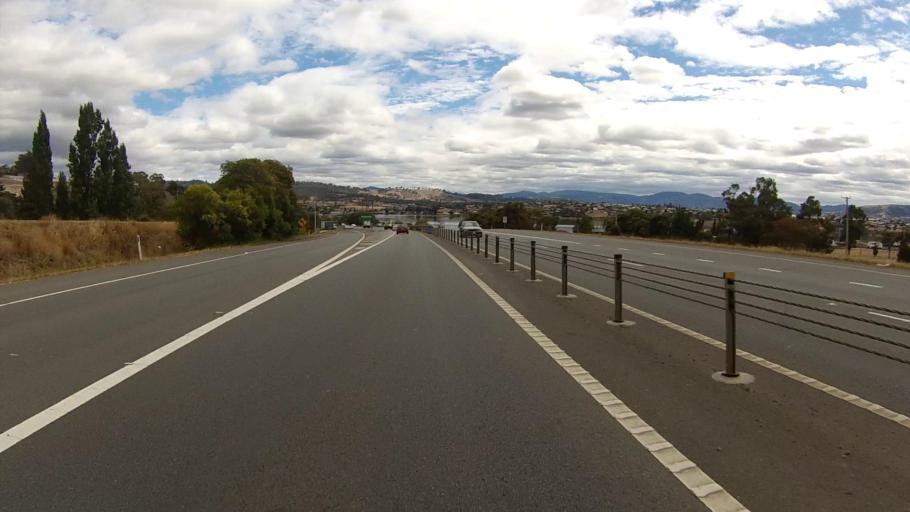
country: AU
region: Tasmania
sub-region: Glenorchy
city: Granton
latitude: -42.7554
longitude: 147.2300
